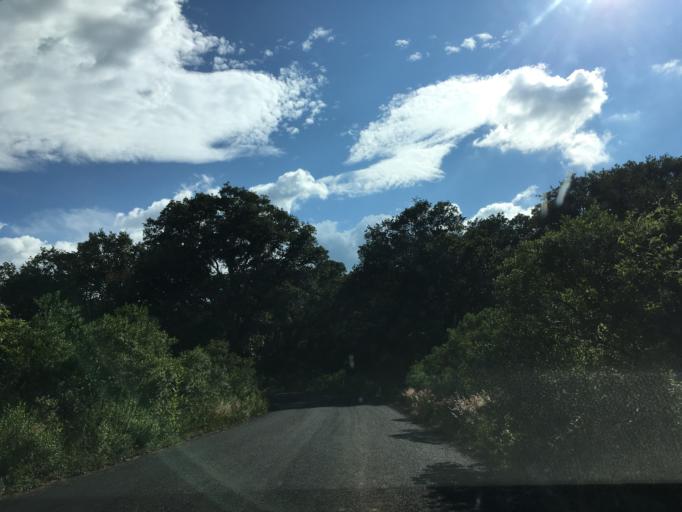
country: MX
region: Michoacan
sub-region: Zacapu
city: Naranja de Tapia
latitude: 19.7535
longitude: -101.7834
